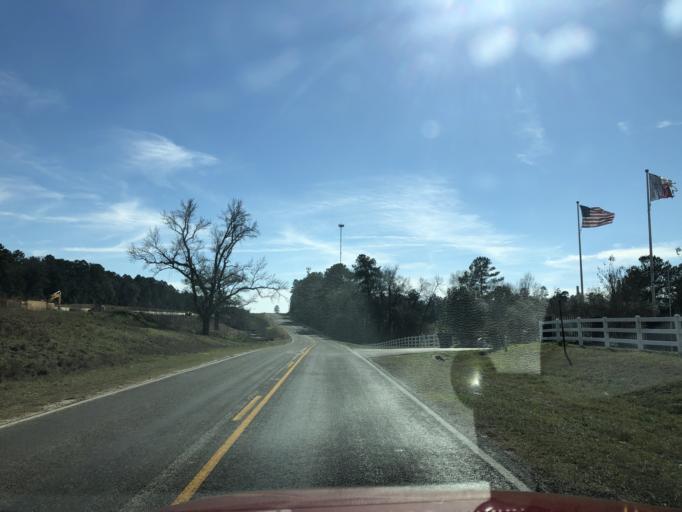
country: US
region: Texas
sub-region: Walker County
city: New Waverly
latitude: 30.6223
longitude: -95.5080
